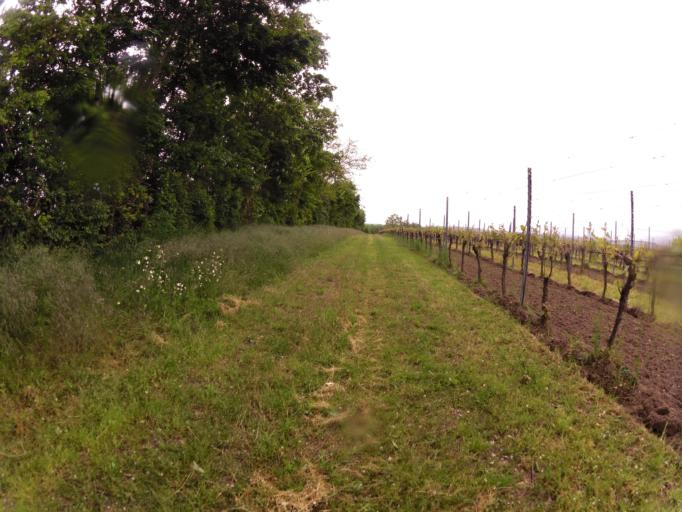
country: DE
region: Bavaria
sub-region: Regierungsbezirk Unterfranken
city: Sommerach
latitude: 49.8471
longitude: 10.2081
